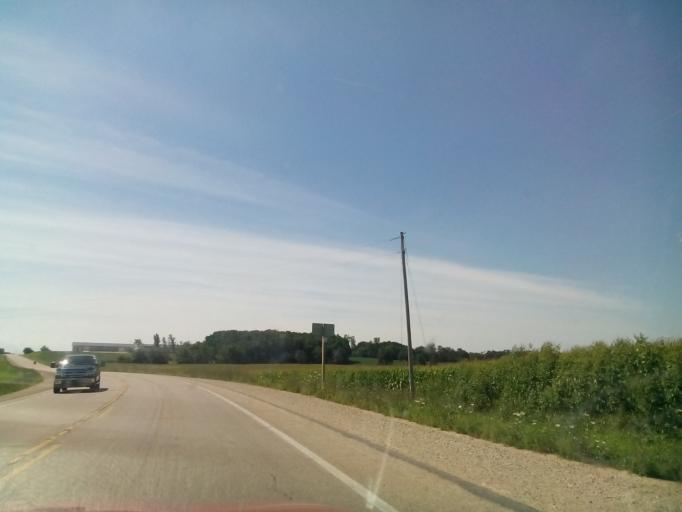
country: US
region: Wisconsin
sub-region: Green County
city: Monticello
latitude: 42.7082
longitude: -89.6172
